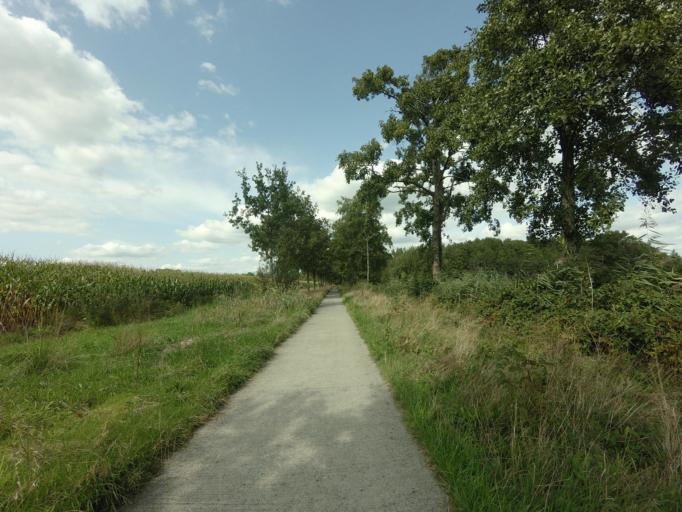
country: NL
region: Drenthe
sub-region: Gemeente Westerveld
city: Havelte
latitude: 52.6944
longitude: 6.2922
